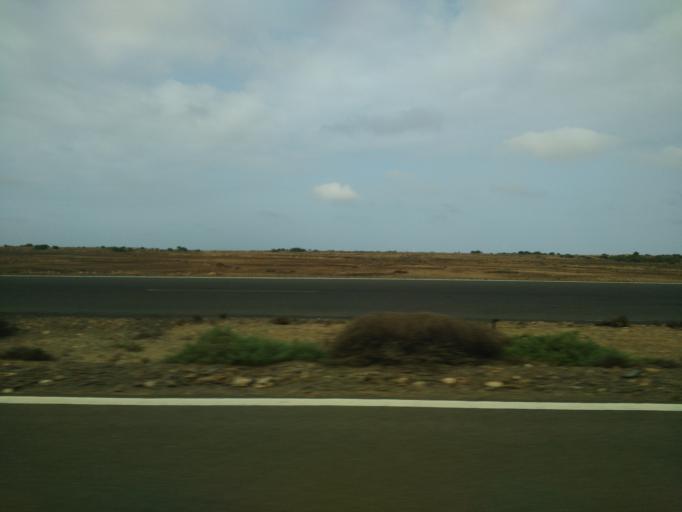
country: CV
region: Sal
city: Espargos
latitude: 16.6849
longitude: -22.9353
